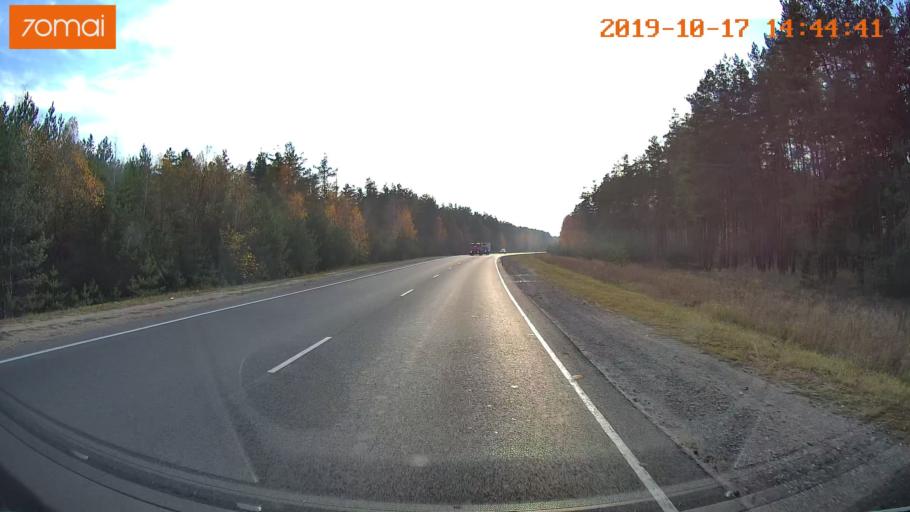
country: RU
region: Rjazan
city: Solotcha
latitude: 54.8092
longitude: 39.8887
